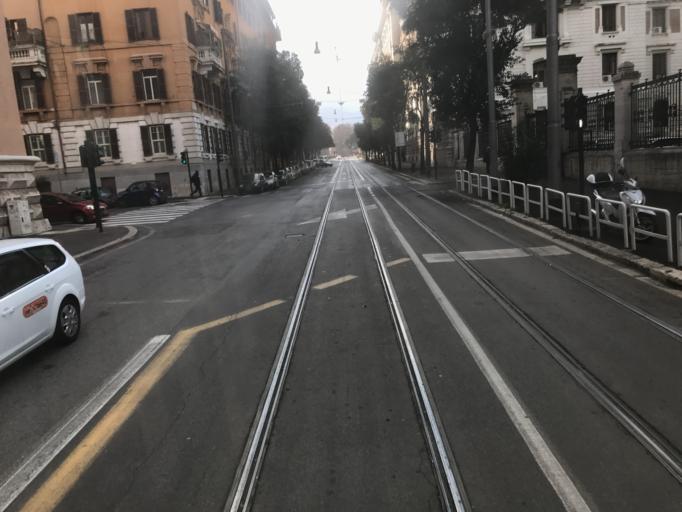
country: VA
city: Vatican City
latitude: 41.9150
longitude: 12.4741
